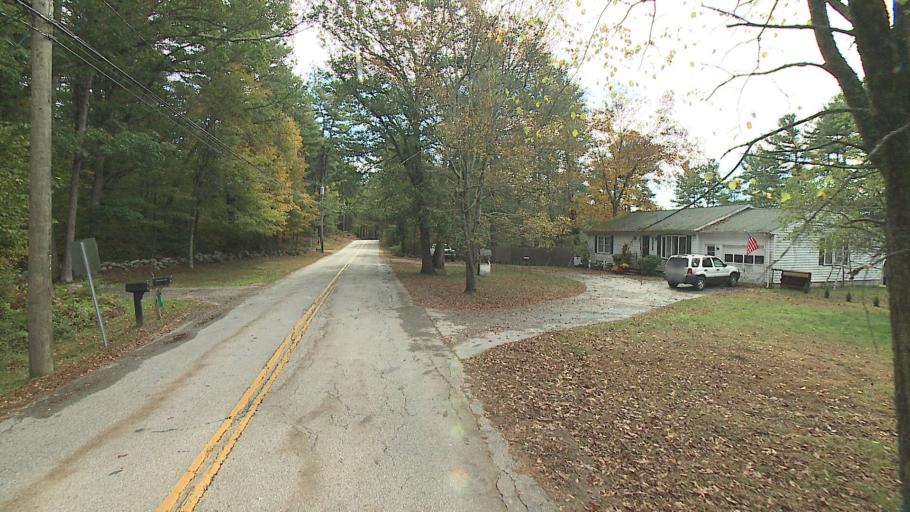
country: US
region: Connecticut
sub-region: Windham County
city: Thompson
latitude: 41.9256
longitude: -71.8218
